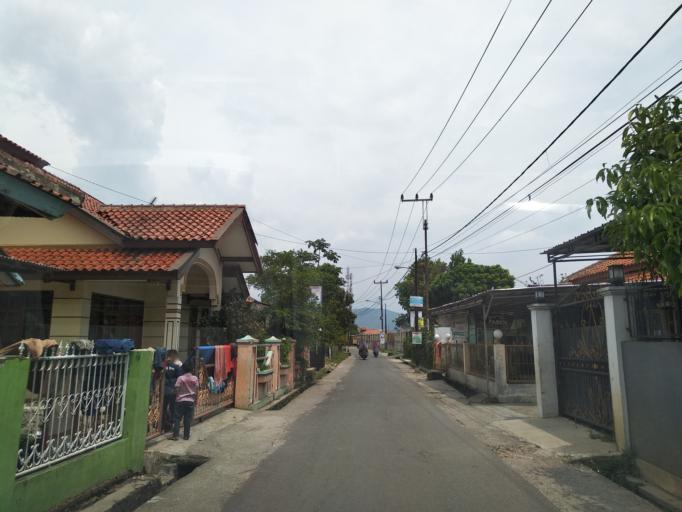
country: ID
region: West Java
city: Pameungpeuk
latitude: -6.9723
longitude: 107.6480
